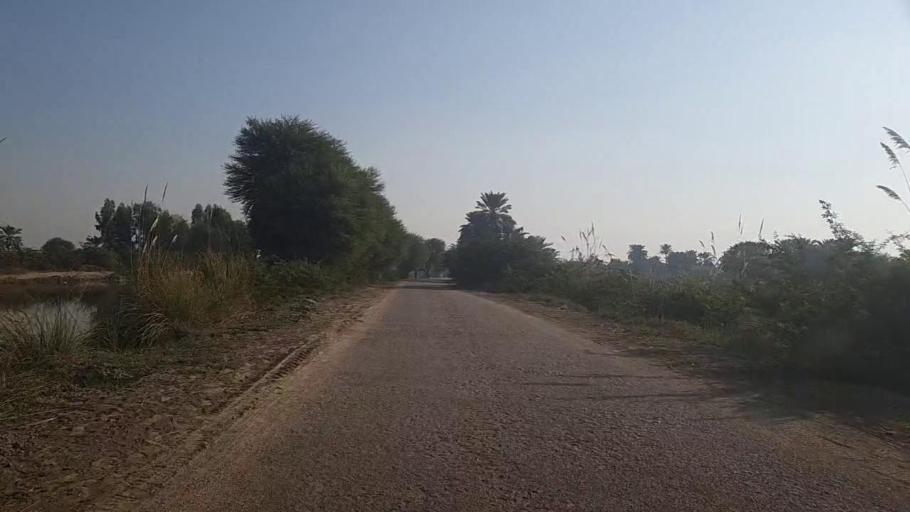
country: PK
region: Sindh
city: Bozdar
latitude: 27.2583
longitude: 68.6760
